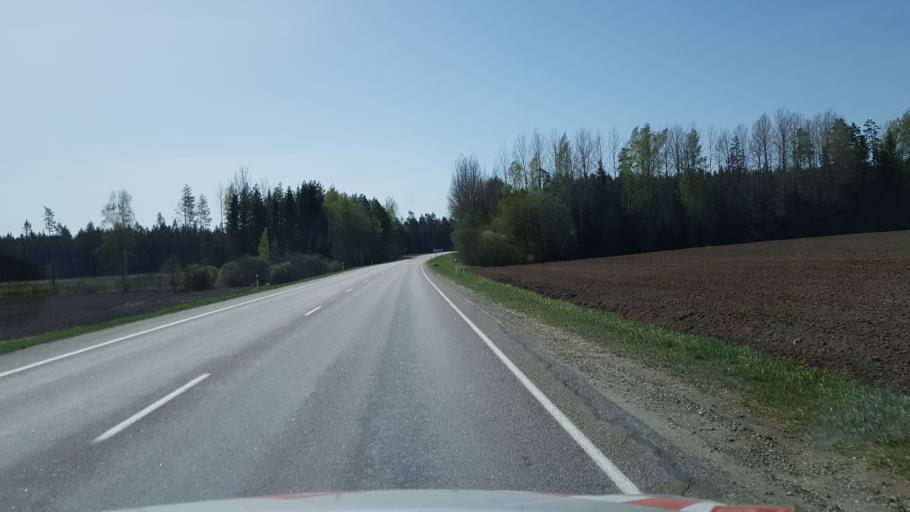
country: EE
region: Valgamaa
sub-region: Valga linn
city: Valga
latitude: 57.8579
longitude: 26.0591
